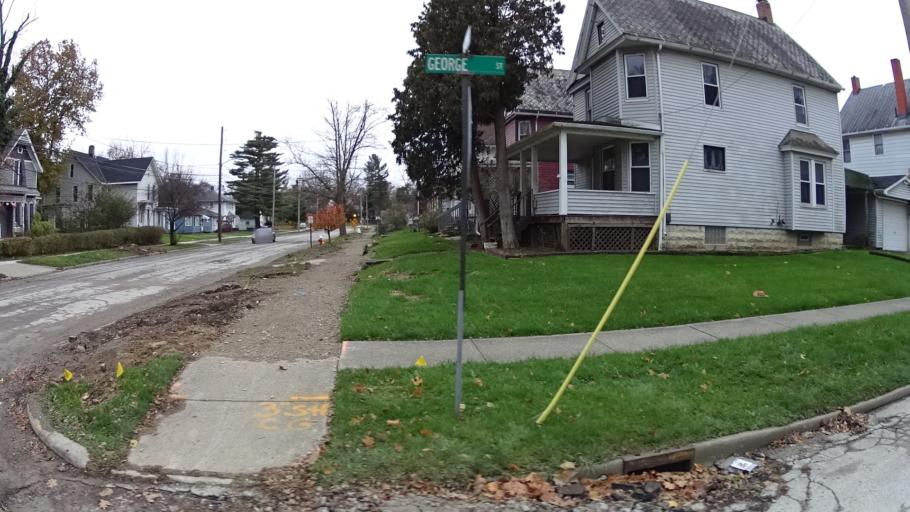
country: US
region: Ohio
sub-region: Lorain County
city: Elyria
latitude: 41.3560
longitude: -82.1042
